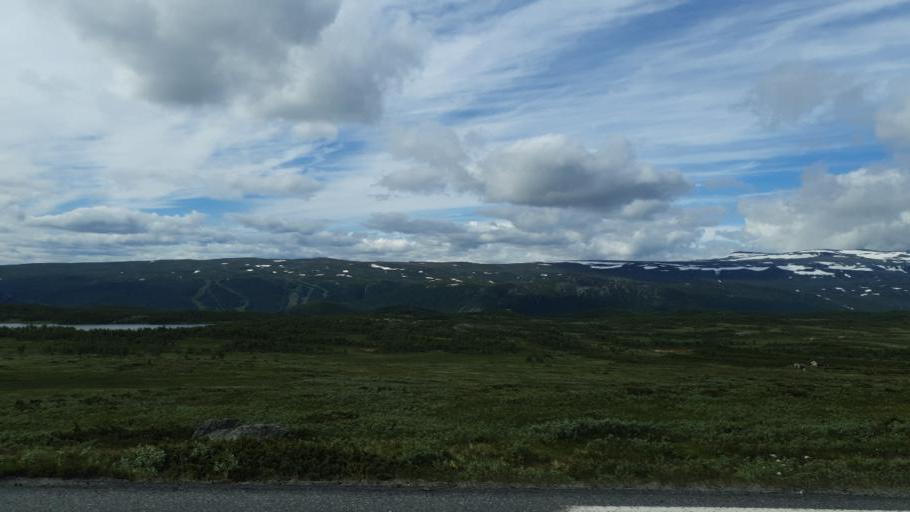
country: NO
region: Oppland
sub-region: Vestre Slidre
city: Slidre
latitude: 61.2726
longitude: 8.8595
